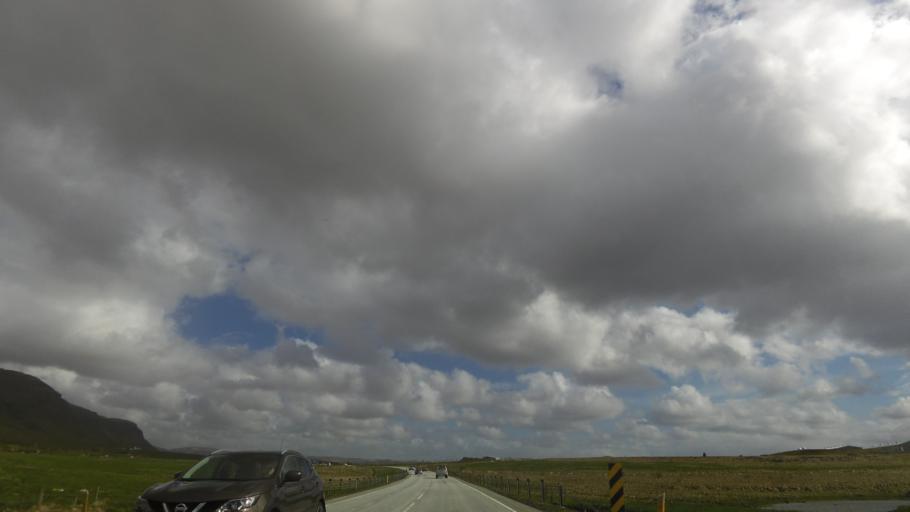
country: IS
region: Capital Region
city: Reykjavik
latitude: 64.2240
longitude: -21.8104
